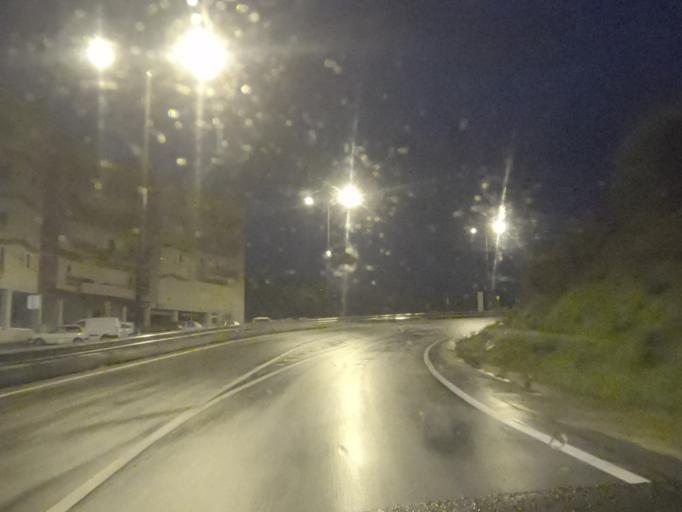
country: PT
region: Vila Real
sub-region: Peso da Regua
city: Peso da Regua
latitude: 41.1668
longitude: -7.7791
